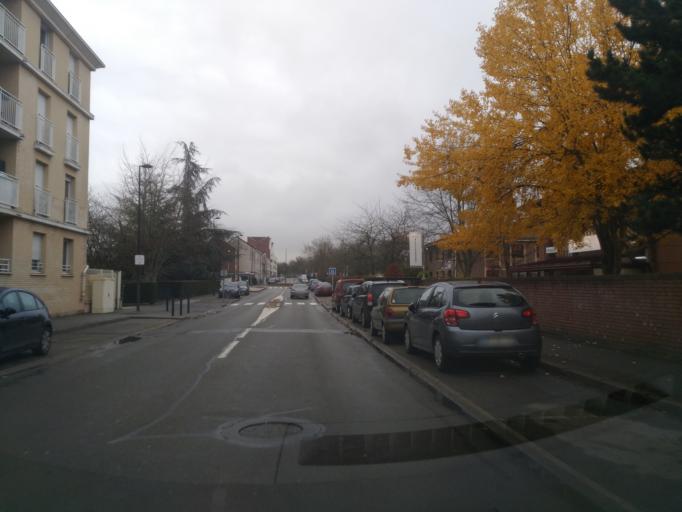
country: FR
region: Ile-de-France
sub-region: Departement des Yvelines
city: Voisins-le-Bretonneux
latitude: 48.7655
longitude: 2.0589
